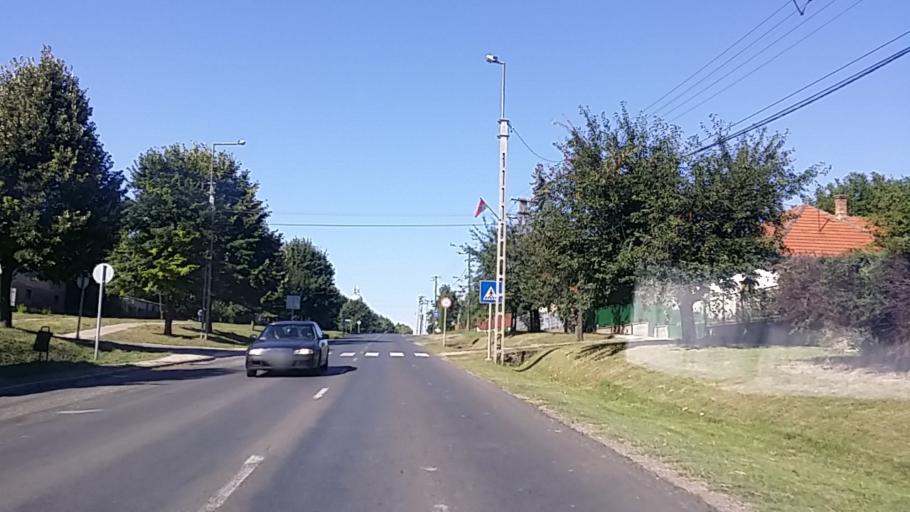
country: HU
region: Fejer
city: dunaujvaros
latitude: 46.9573
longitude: 18.8627
